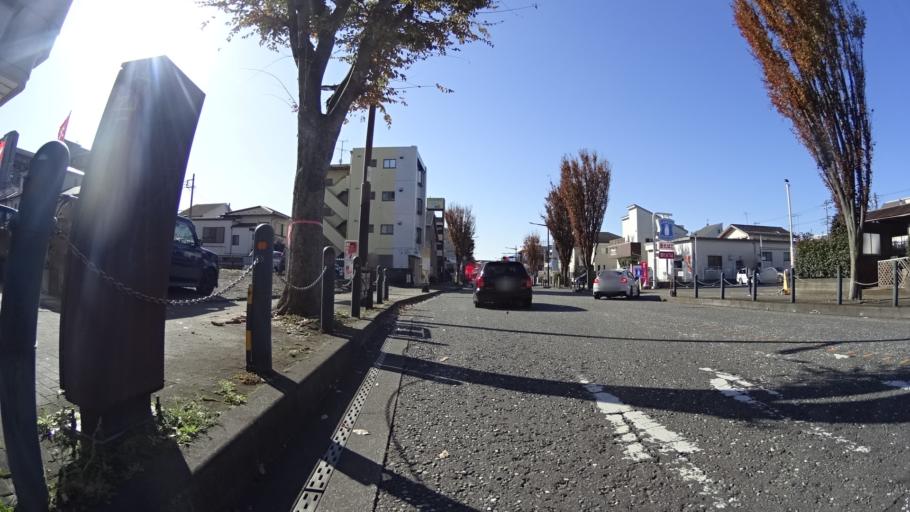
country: JP
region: Kanagawa
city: Zama
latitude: 35.5699
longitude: 139.3624
